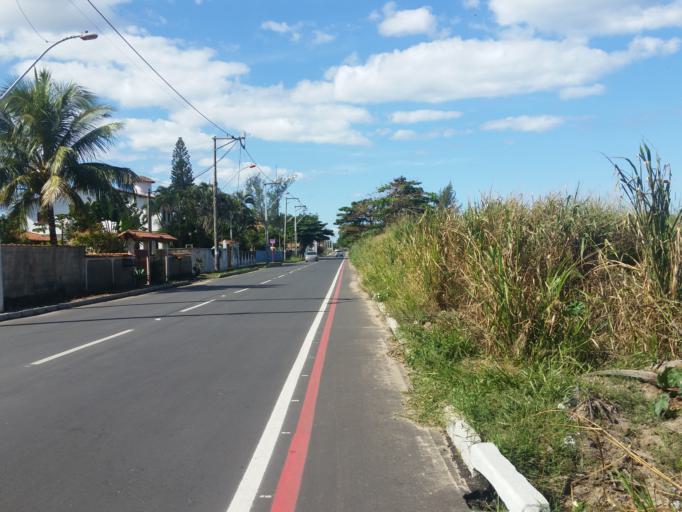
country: BR
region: Rio de Janeiro
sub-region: Marica
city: Marica
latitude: -22.9679
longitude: -42.9658
